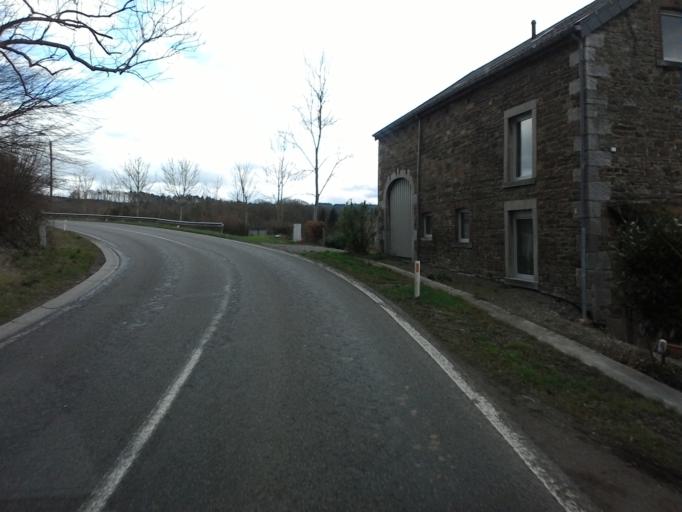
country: BE
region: Wallonia
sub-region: Province de Liege
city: Ferrieres
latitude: 50.4022
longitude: 5.6182
